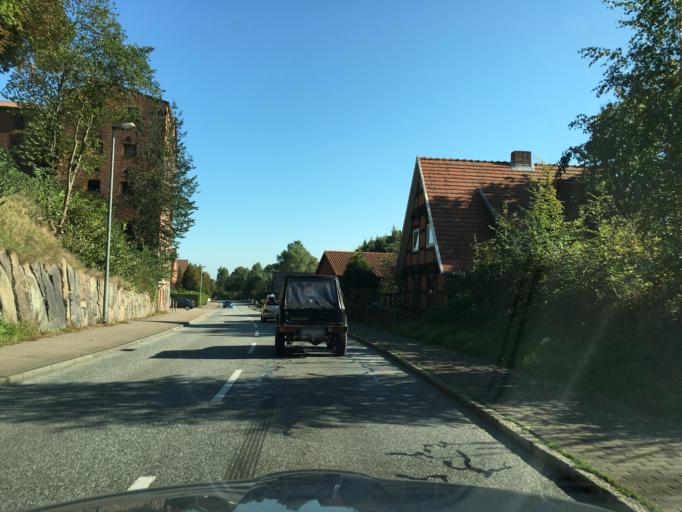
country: DE
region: Schleswig-Holstein
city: Buchhorst
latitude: 53.3727
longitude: 10.5716
